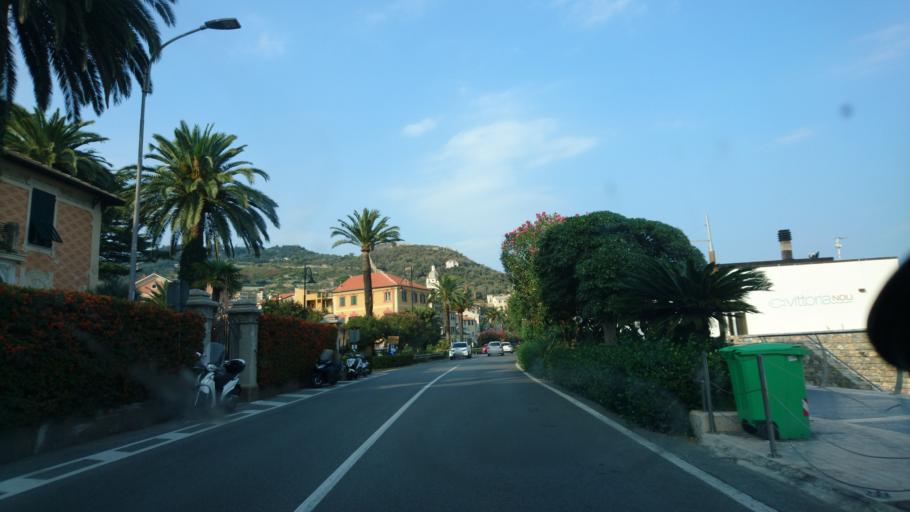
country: IT
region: Liguria
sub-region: Provincia di Savona
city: Noli
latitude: 44.2030
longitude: 8.4158
